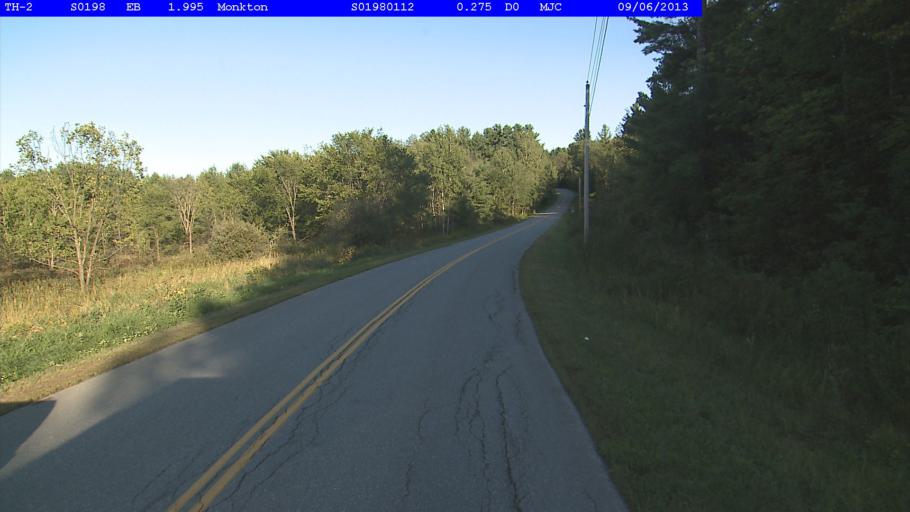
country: US
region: Vermont
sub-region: Chittenden County
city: Hinesburg
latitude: 44.2553
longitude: -73.1895
